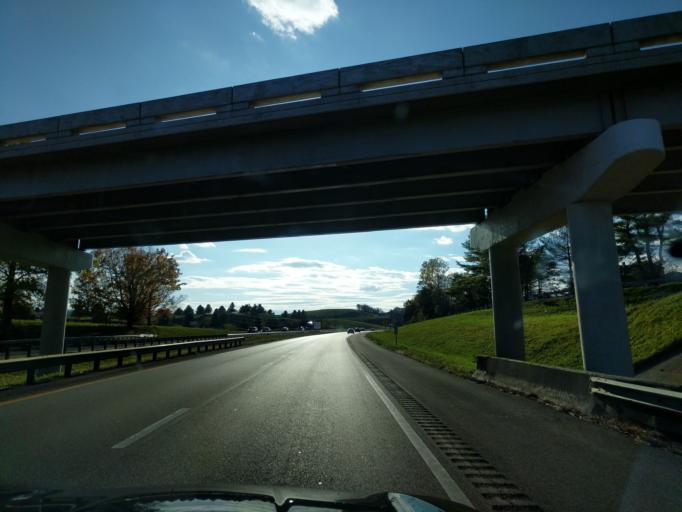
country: US
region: Virginia
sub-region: Washington County
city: Glade Spring
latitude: 36.7832
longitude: -81.7350
